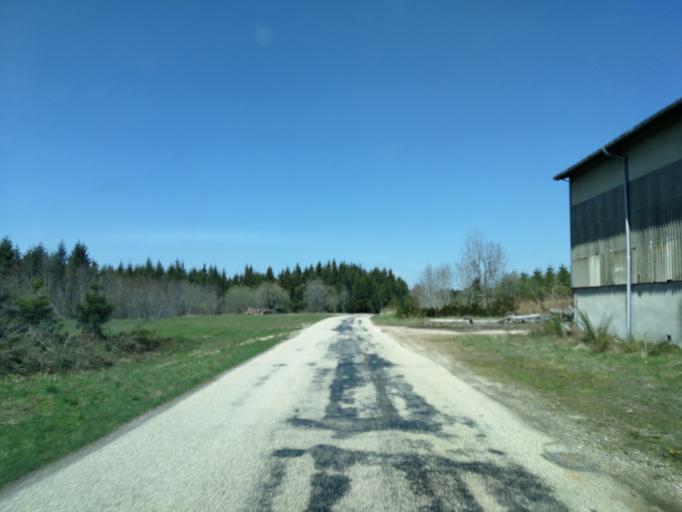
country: FR
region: Auvergne
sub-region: Departement de la Haute-Loire
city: Montfaucon-en-Velay
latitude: 45.1294
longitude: 4.3972
